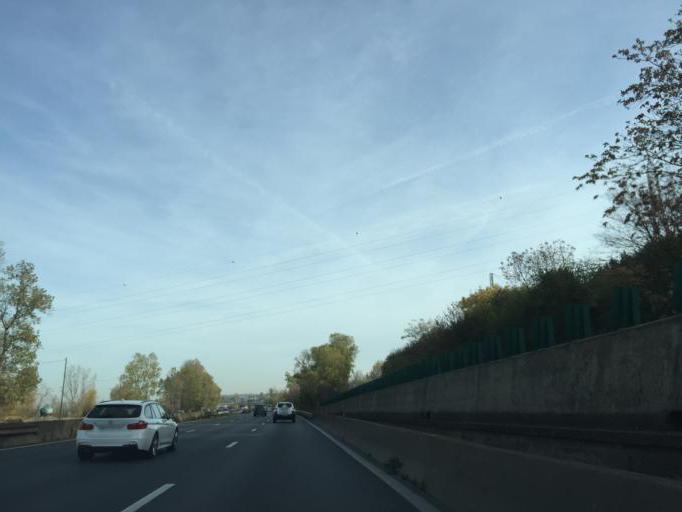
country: FR
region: Rhone-Alpes
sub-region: Departement du Rhone
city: Ternay
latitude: 45.6099
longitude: 4.8056
